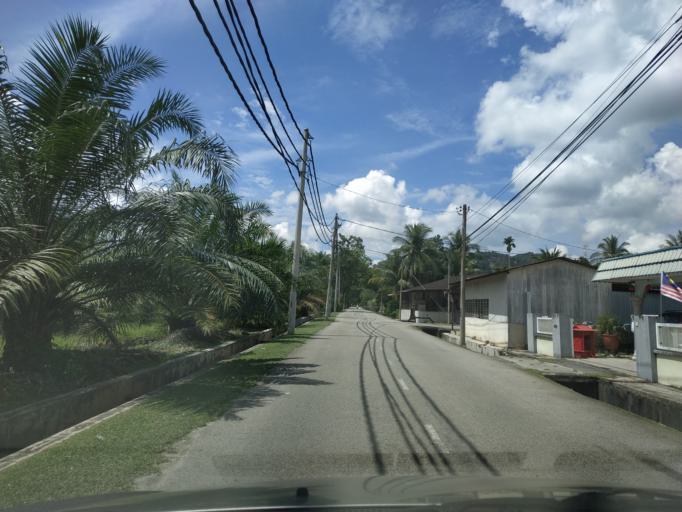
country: MY
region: Perak
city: Parit Buntar
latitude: 5.1383
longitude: 100.5922
